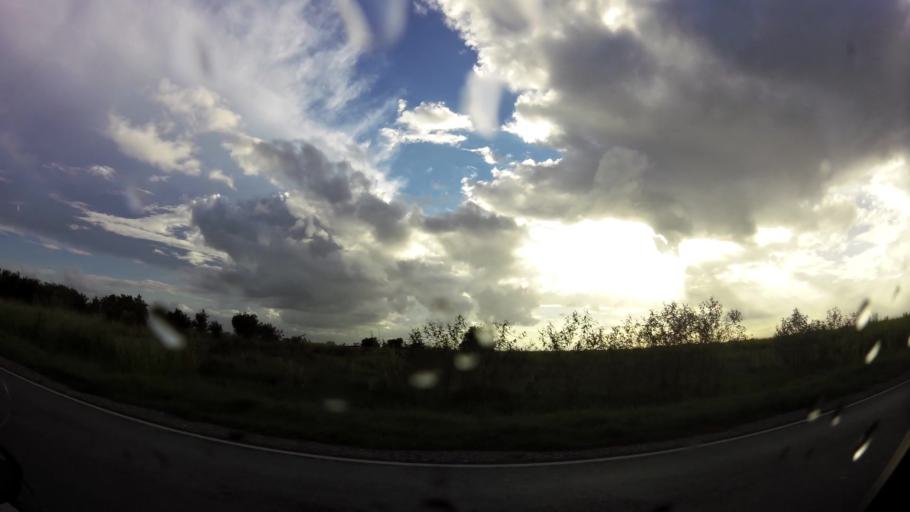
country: TT
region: Tunapuna/Piarco
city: Tunapuna
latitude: 10.5990
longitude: -61.3717
